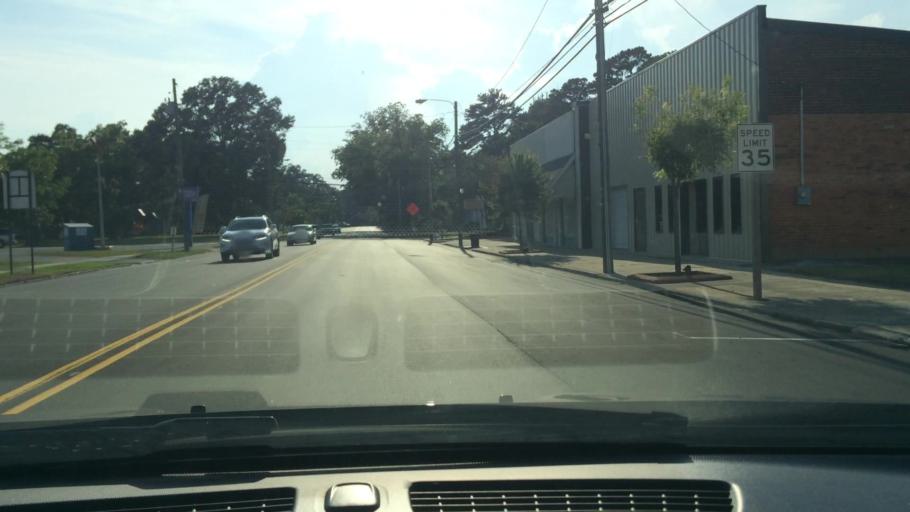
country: US
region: North Carolina
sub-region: Pitt County
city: Ayden
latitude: 35.4712
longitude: -77.4190
